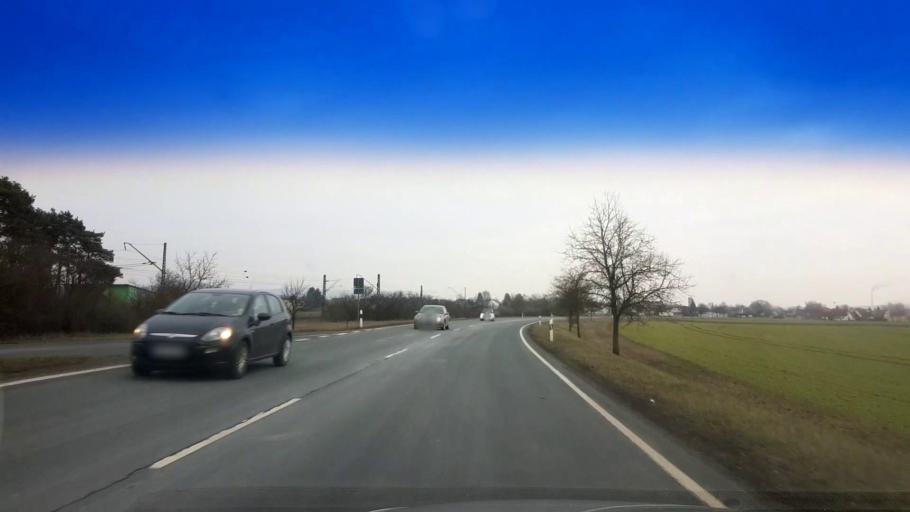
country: DE
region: Bavaria
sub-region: Upper Franconia
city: Altendorf
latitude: 49.8068
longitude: 11.0045
